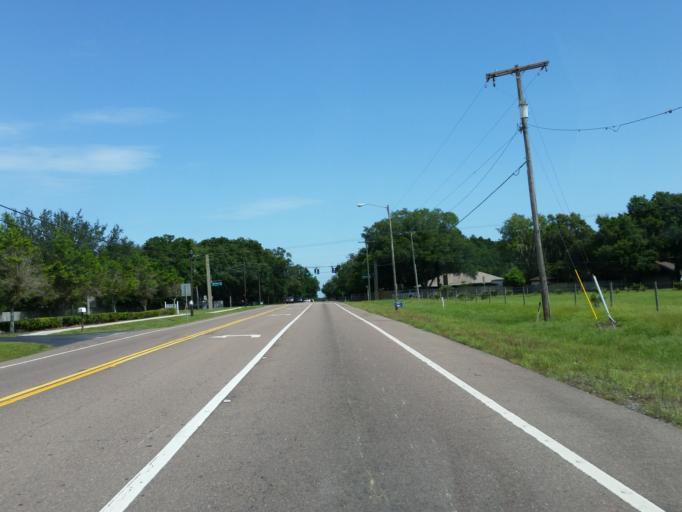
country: US
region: Florida
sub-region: Hillsborough County
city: Bloomingdale
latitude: 27.9072
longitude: -82.2557
